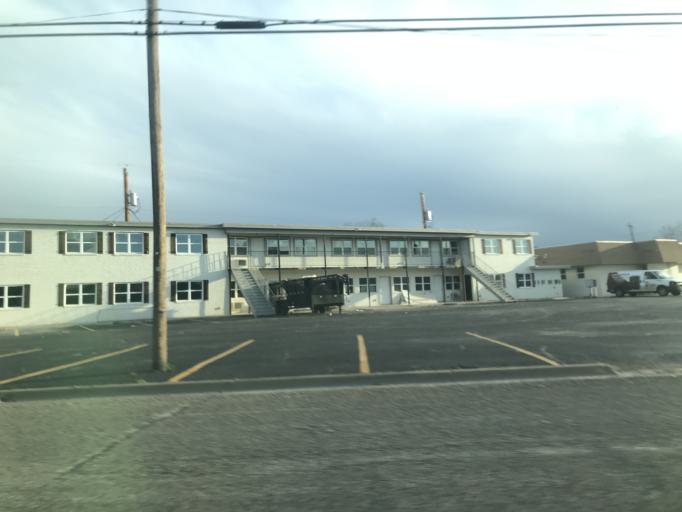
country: US
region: Texas
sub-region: Tom Green County
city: San Angelo
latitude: 31.4973
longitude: -100.4584
